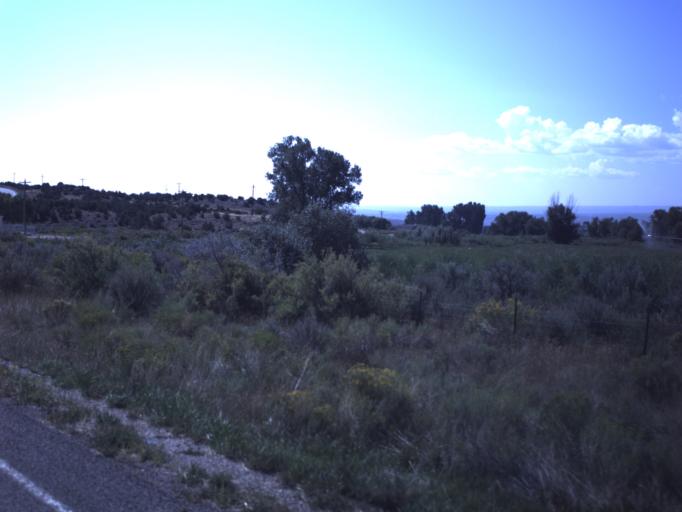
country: US
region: Utah
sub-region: Duchesne County
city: Duchesne
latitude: 40.2601
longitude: -110.4090
